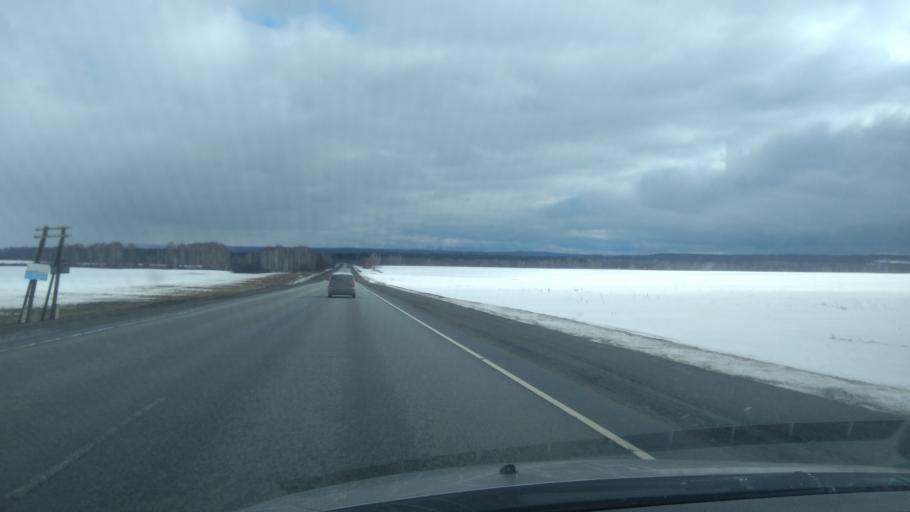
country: RU
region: Sverdlovsk
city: Ufimskiy
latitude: 56.7730
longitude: 58.0671
